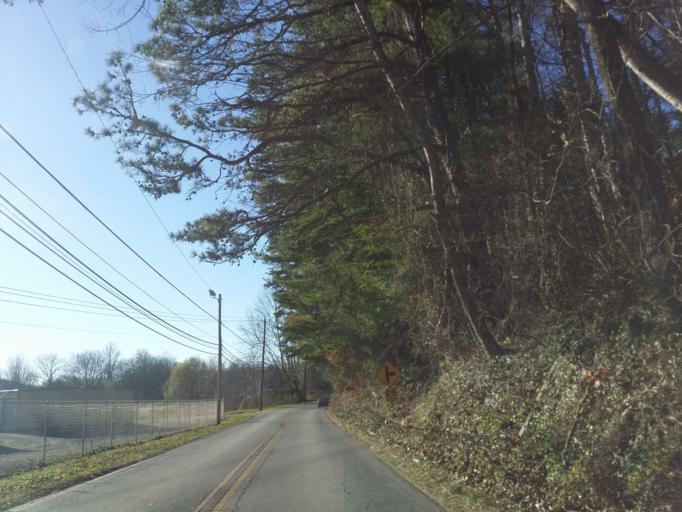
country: US
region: North Carolina
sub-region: Buncombe County
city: Swannanoa
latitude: 35.6120
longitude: -82.4177
